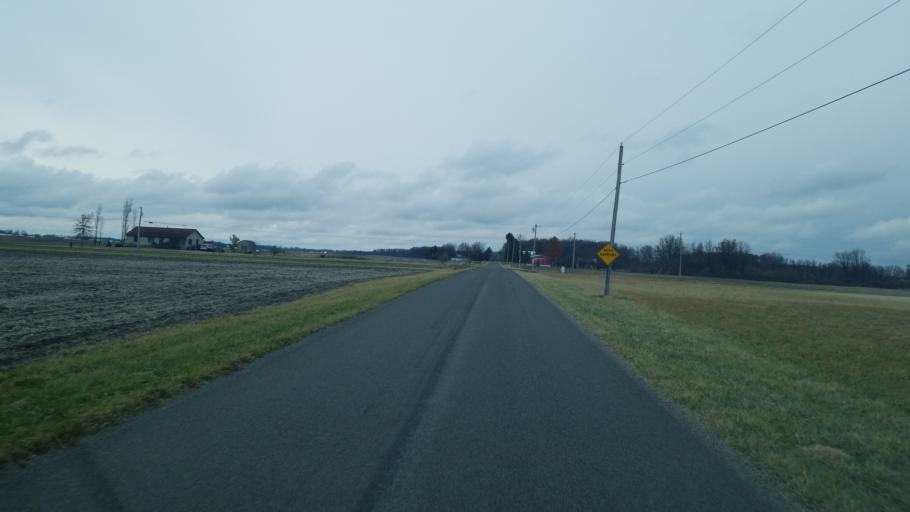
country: US
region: Ohio
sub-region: Union County
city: Richwood
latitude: 40.3143
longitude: -83.2513
